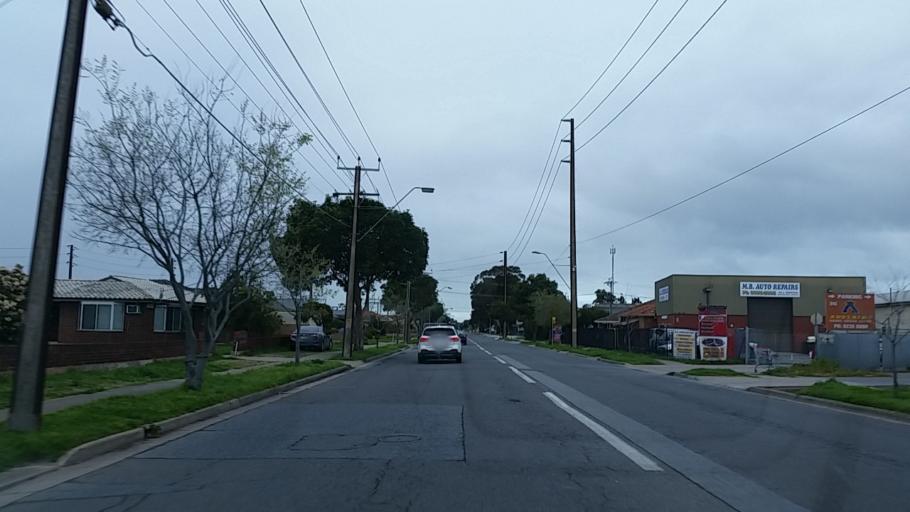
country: AU
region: South Australia
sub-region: Charles Sturt
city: Findon
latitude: -34.9068
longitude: 138.5328
